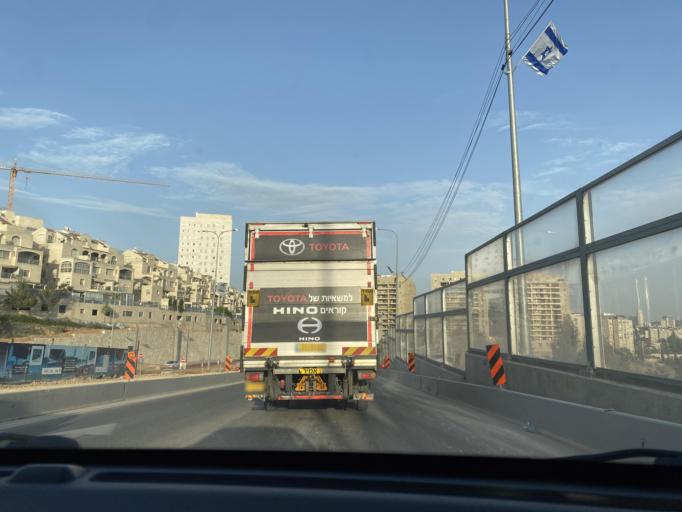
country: IL
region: Jerusalem
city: Jerusalem
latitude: 31.7679
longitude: 35.1902
